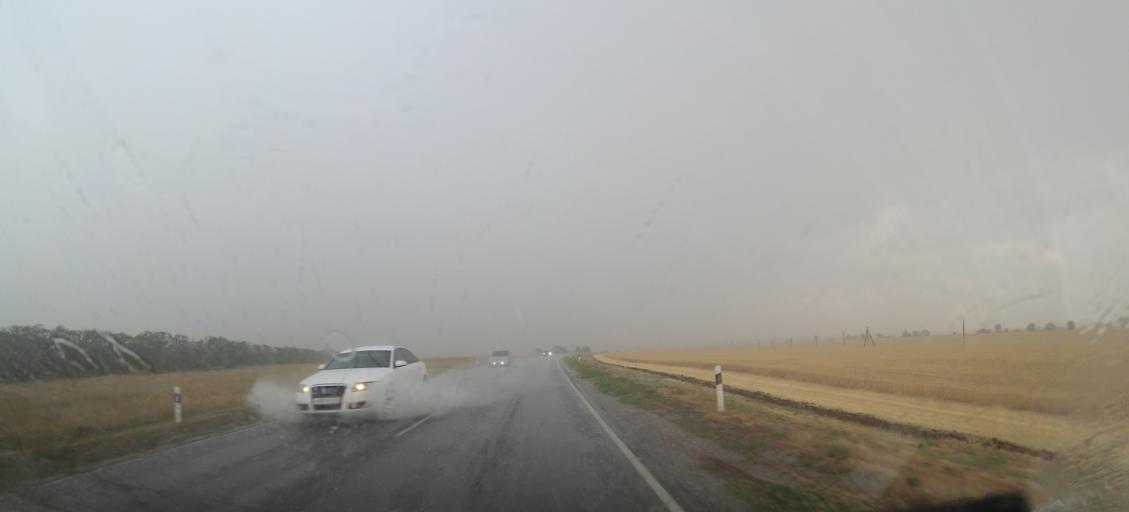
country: RU
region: Rostov
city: Proletarsk
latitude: 46.6728
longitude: 41.6955
